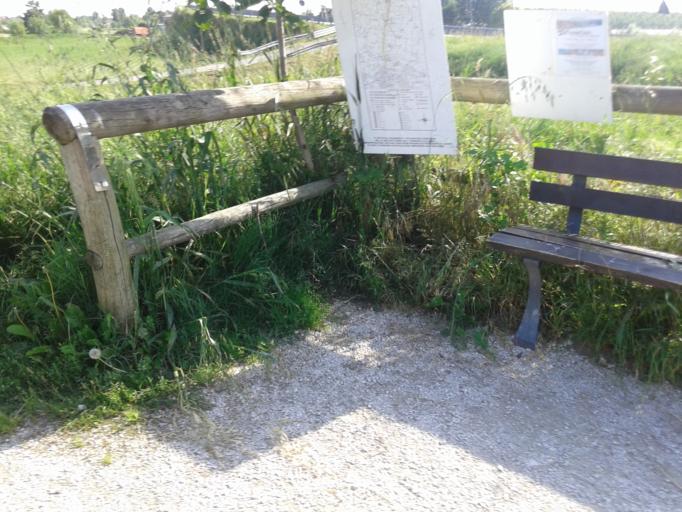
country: IT
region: Veneto
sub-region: Provincia di Padova
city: Loreggiola
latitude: 45.6138
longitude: 11.9288
